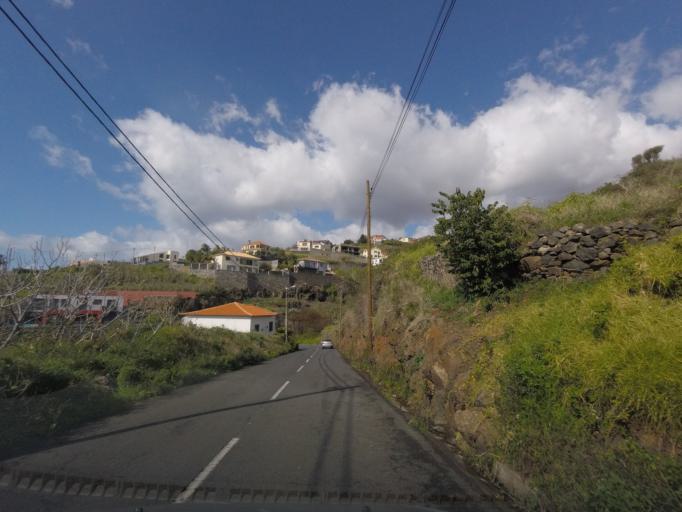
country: PT
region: Madeira
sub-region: Calheta
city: Estreito da Calheta
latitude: 32.7334
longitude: -17.1962
